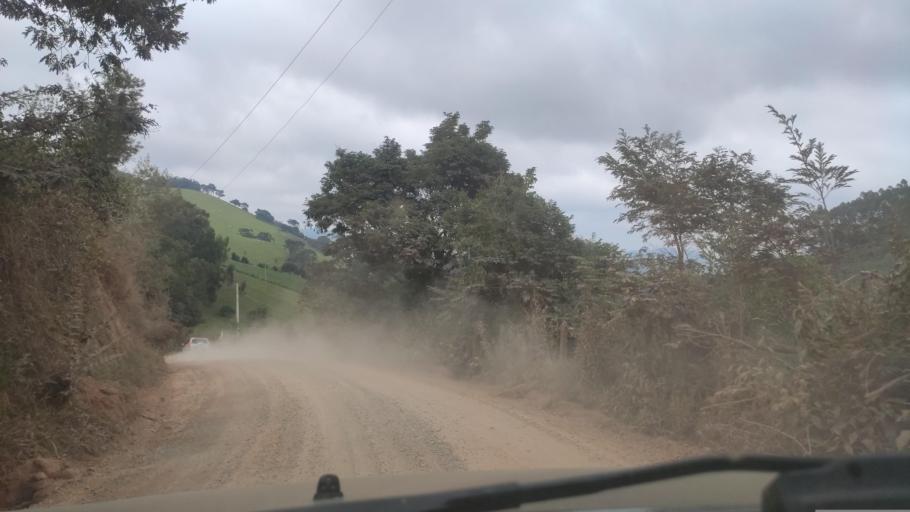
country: BR
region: Minas Gerais
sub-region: Paraisopolis
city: Paraisopolis
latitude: -22.6614
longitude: -45.8778
